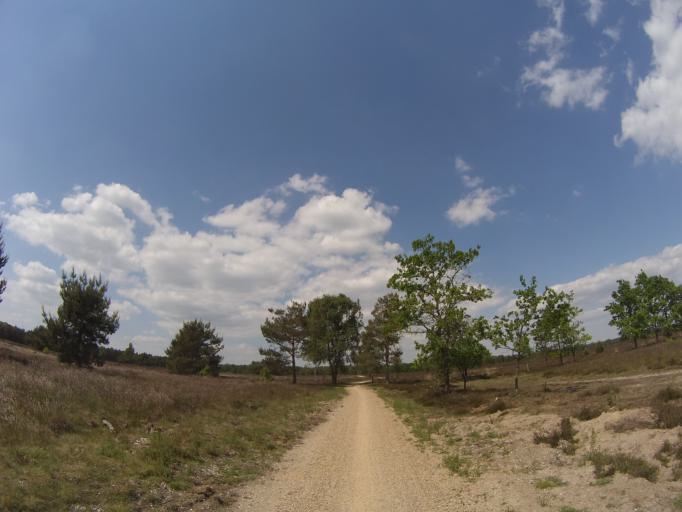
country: NL
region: Gelderland
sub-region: Gemeente Barneveld
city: Stroe
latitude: 52.1820
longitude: 5.7129
